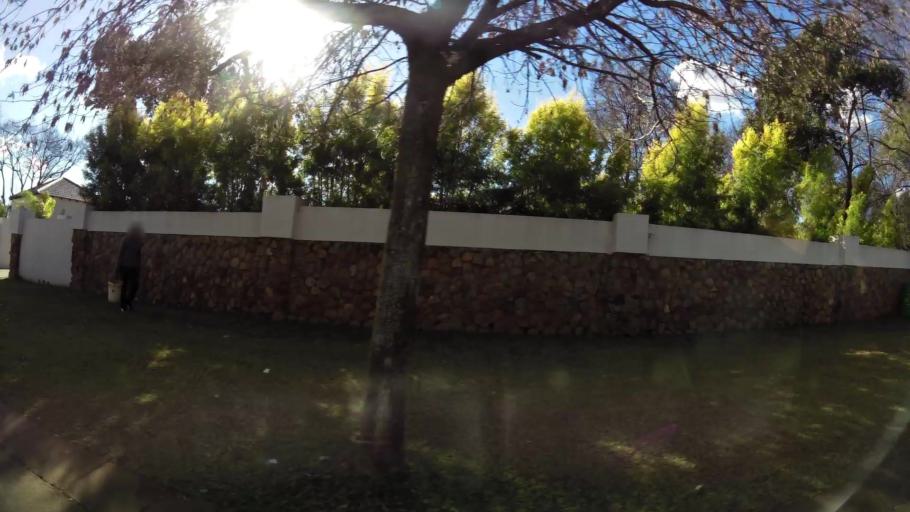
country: ZA
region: North-West
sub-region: Dr Kenneth Kaunda District Municipality
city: Klerksdorp
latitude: -26.8282
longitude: 26.6700
